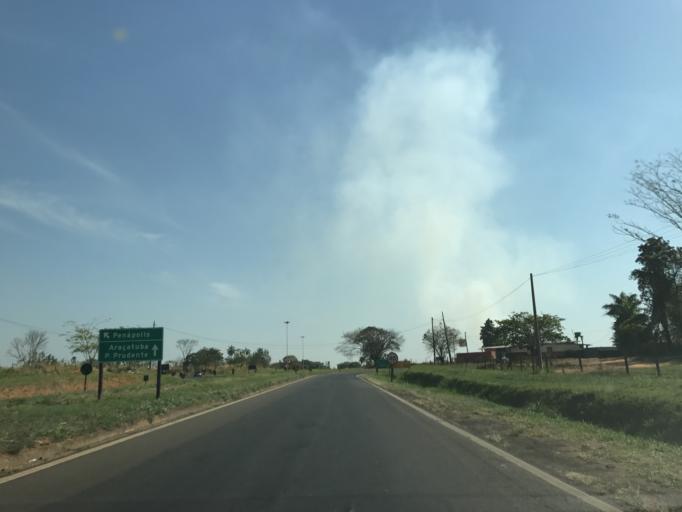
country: BR
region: Sao Paulo
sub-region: Penapolis
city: Penapolis
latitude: -21.3854
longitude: -50.0951
